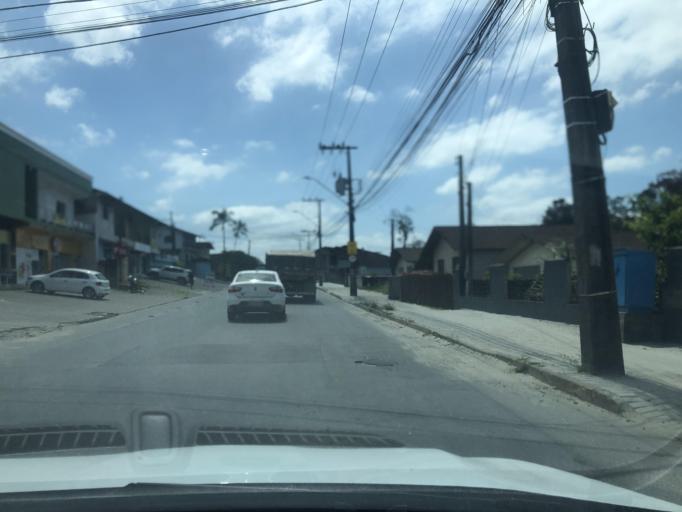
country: BR
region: Santa Catarina
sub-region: Joinville
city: Joinville
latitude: -26.3394
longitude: -48.8003
